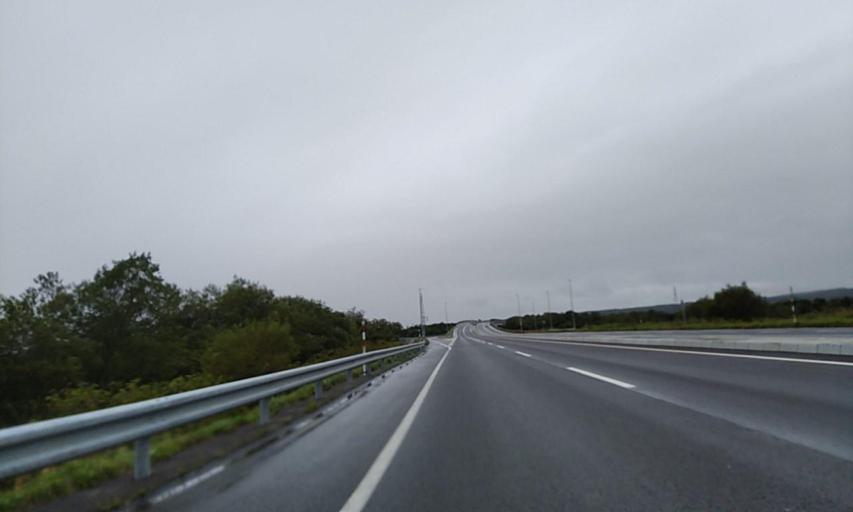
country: JP
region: Hokkaido
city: Kushiro
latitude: 43.0255
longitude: 144.2869
